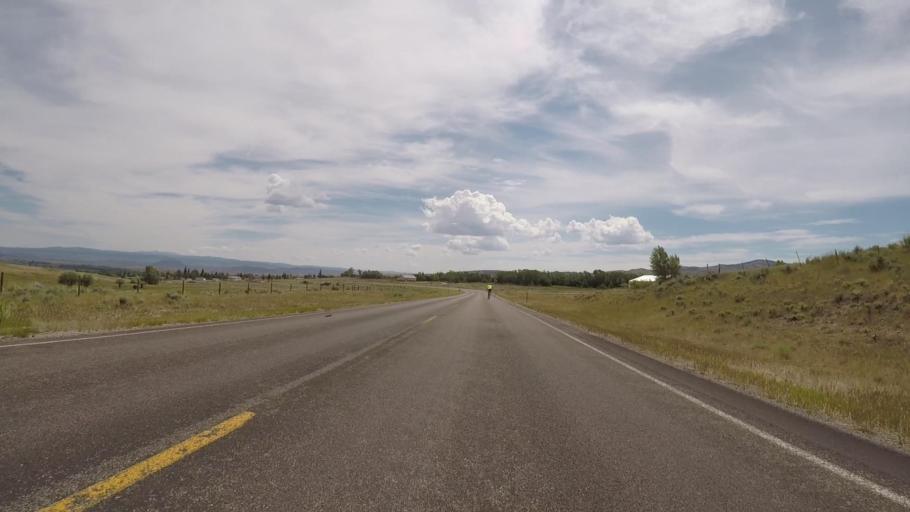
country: US
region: Wyoming
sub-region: Carbon County
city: Saratoga
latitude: 41.2044
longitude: -106.8069
